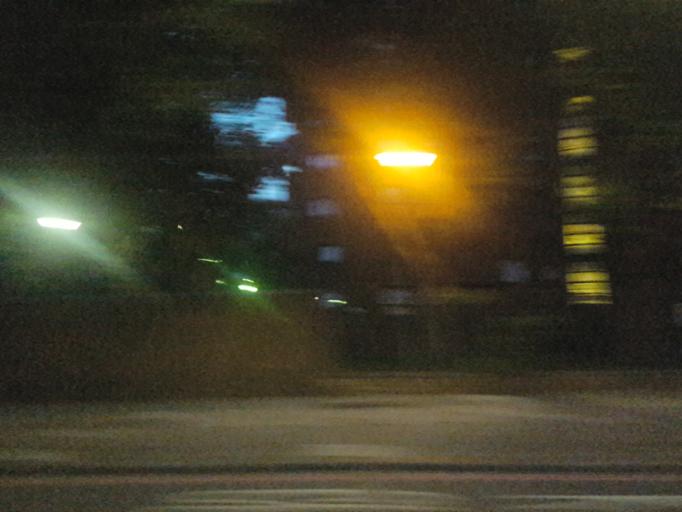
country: GB
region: England
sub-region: Greater London
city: Chelsea
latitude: 51.4803
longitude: -0.1785
